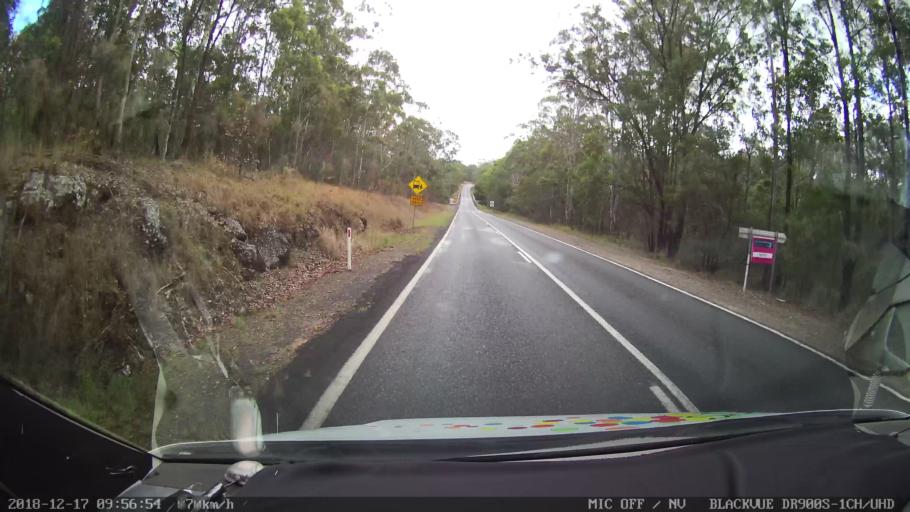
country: AU
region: New South Wales
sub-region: Tenterfield Municipality
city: Carrolls Creek
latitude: -28.9296
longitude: 152.3923
